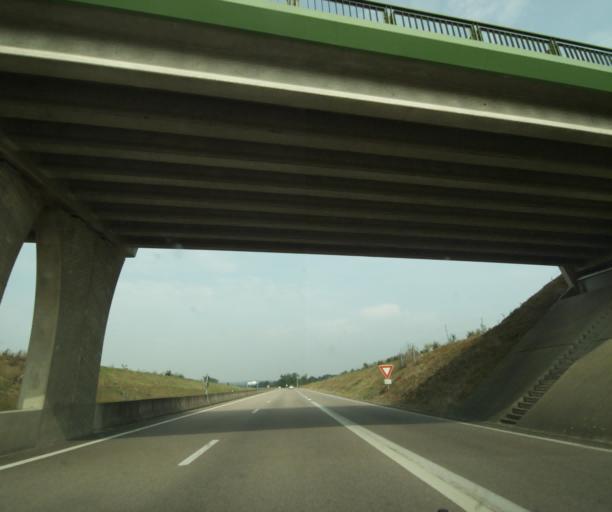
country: FR
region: Lower Normandy
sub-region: Departement du Calvados
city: Falaise
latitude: 48.8542
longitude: -0.1783
